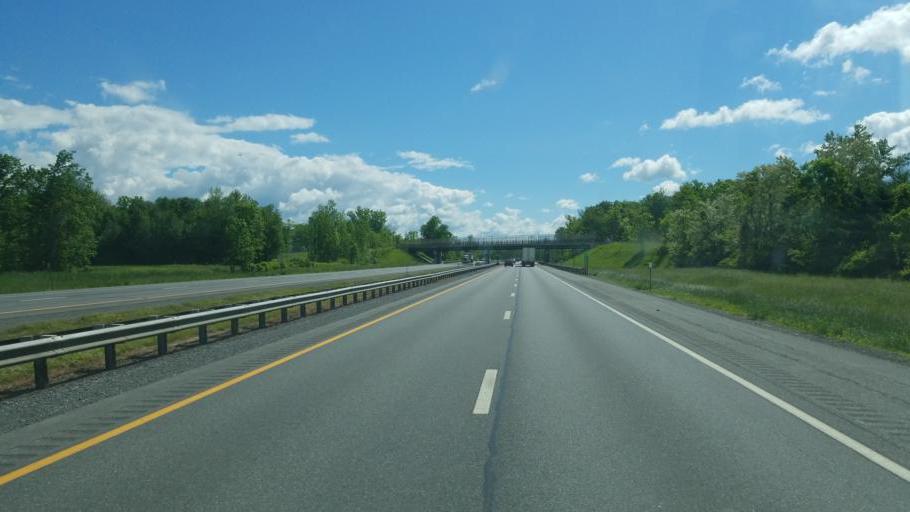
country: US
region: New York
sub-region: Madison County
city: Oneida
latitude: 43.1065
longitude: -75.6828
